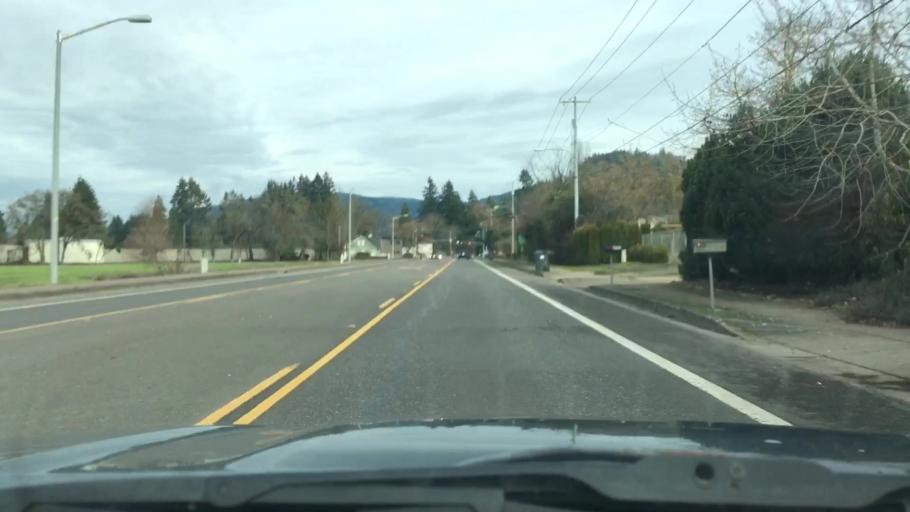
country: US
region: Oregon
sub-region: Lane County
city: Coburg
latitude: 44.1027
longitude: -123.0602
